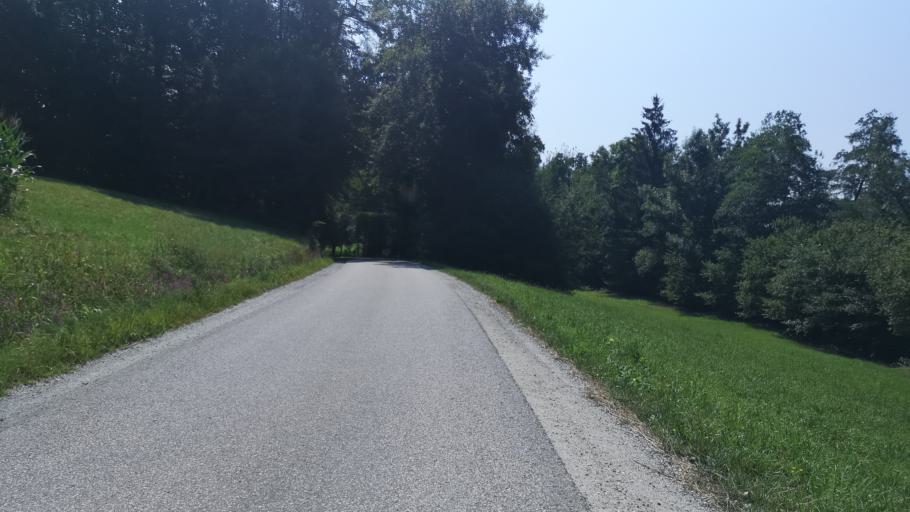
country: AT
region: Styria
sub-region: Politischer Bezirk Deutschlandsberg
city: Preding
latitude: 46.8836
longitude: 15.3740
